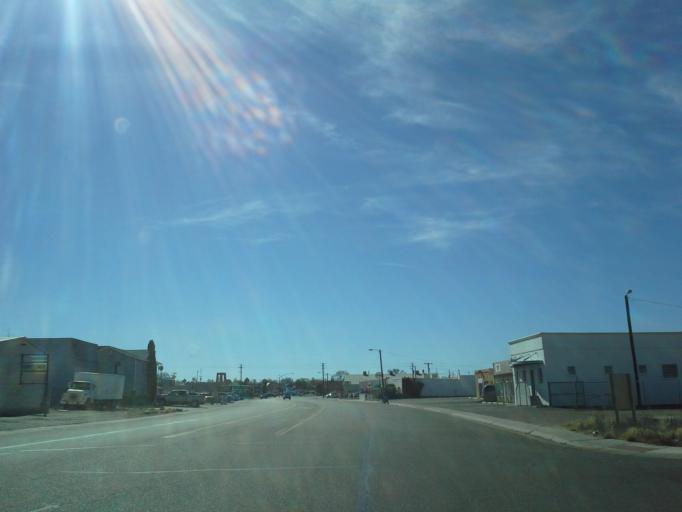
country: US
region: Arizona
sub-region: Coconino County
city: Page
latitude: 36.9216
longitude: -111.4579
